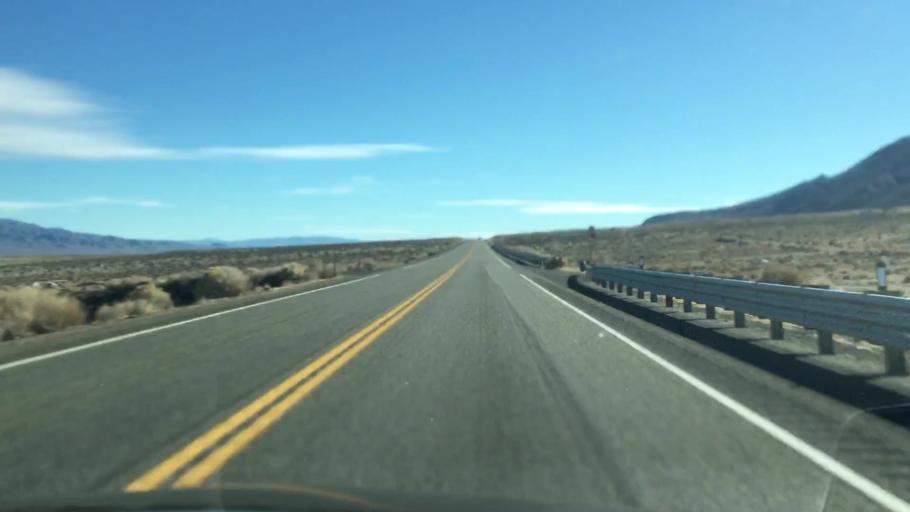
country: US
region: Nevada
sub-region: Mineral County
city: Hawthorne
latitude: 38.8111
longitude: -118.7648
